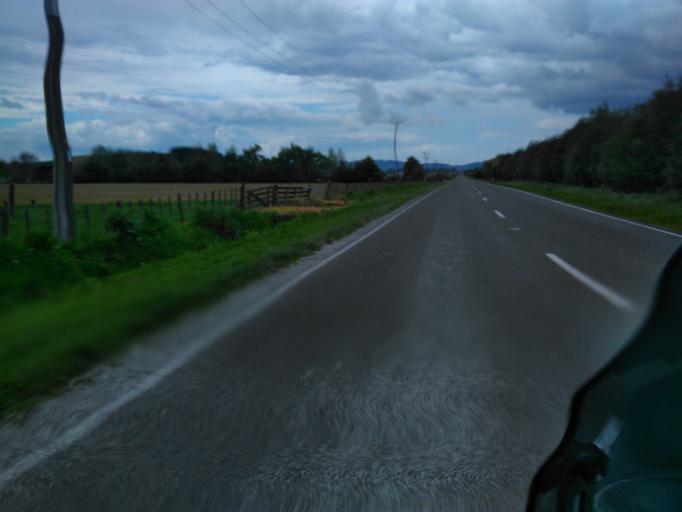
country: NZ
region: Gisborne
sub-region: Gisborne District
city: Gisborne
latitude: -38.6436
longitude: 177.8745
